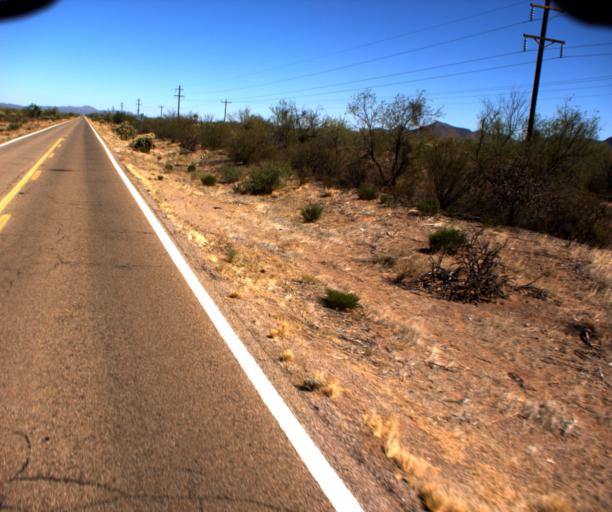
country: US
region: Arizona
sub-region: Pima County
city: Sells
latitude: 31.9954
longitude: -111.9816
